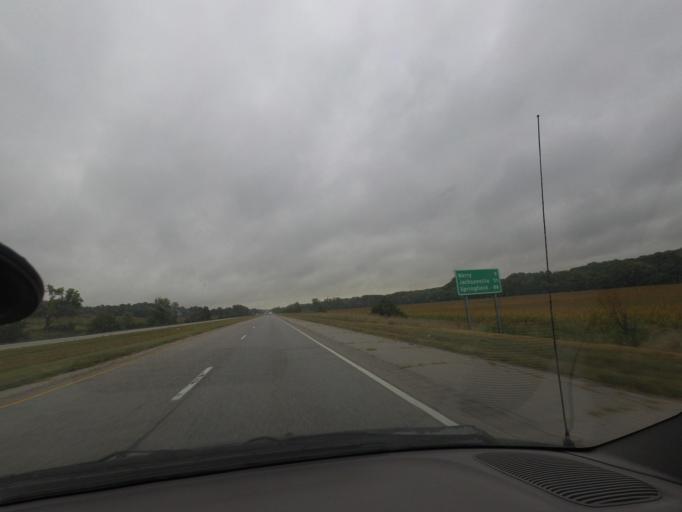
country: US
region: Illinois
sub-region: Adams County
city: Payson
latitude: 39.7206
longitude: -91.1757
